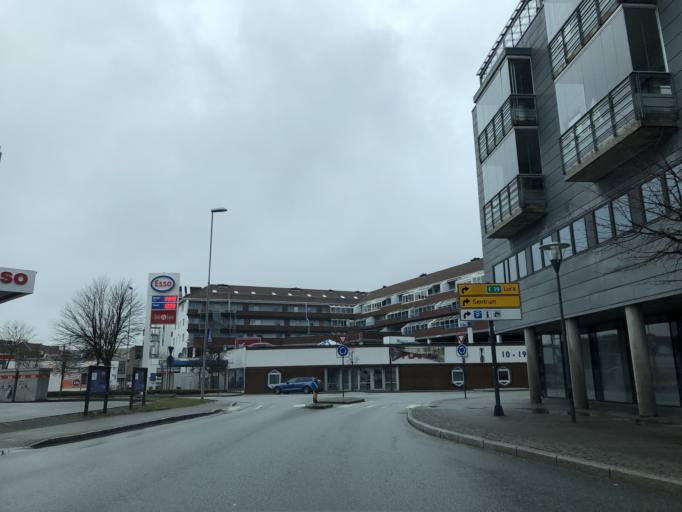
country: NO
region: Rogaland
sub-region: Sandnes
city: Sandnes
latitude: 58.8492
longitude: 5.7375
